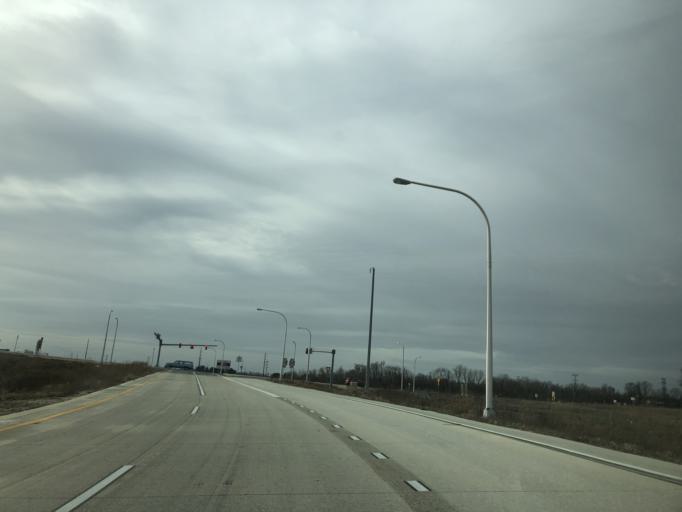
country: US
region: Delaware
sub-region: New Castle County
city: Middletown
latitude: 39.4465
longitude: -75.7520
